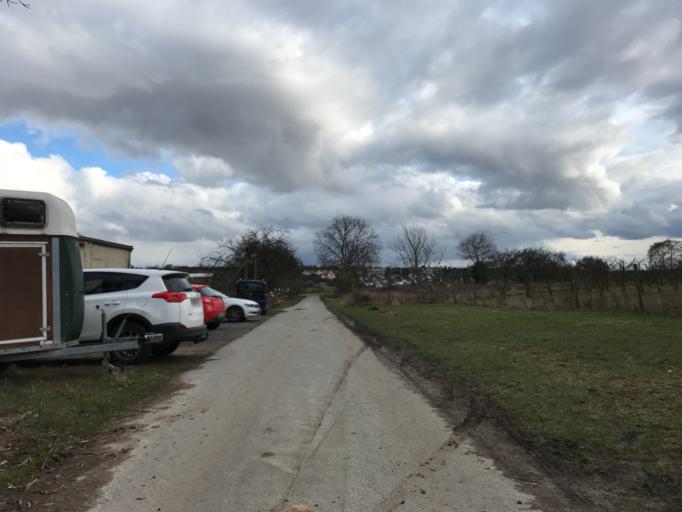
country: DE
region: Hesse
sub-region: Regierungsbezirk Darmstadt
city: Niedernhausen
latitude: 50.0895
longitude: 8.3155
